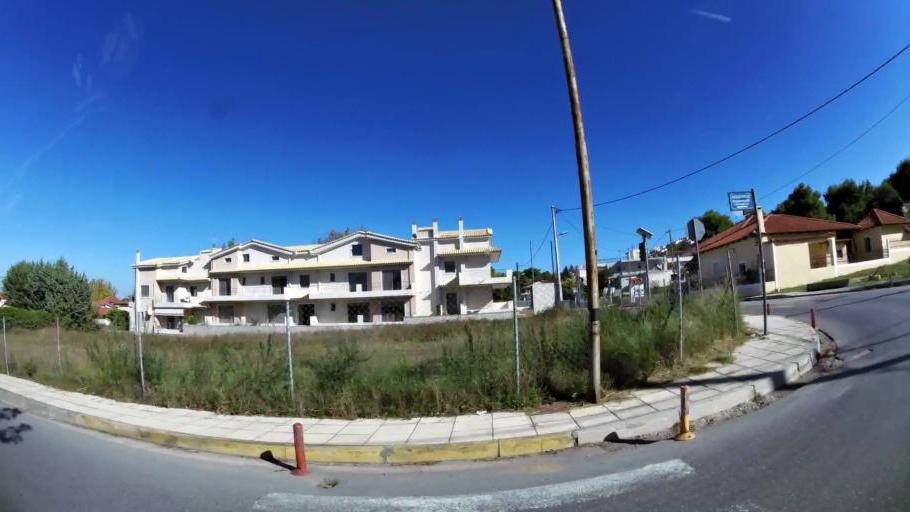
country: GR
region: Attica
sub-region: Nomarchia Anatolikis Attikis
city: Drosia
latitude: 38.1158
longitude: 23.8722
